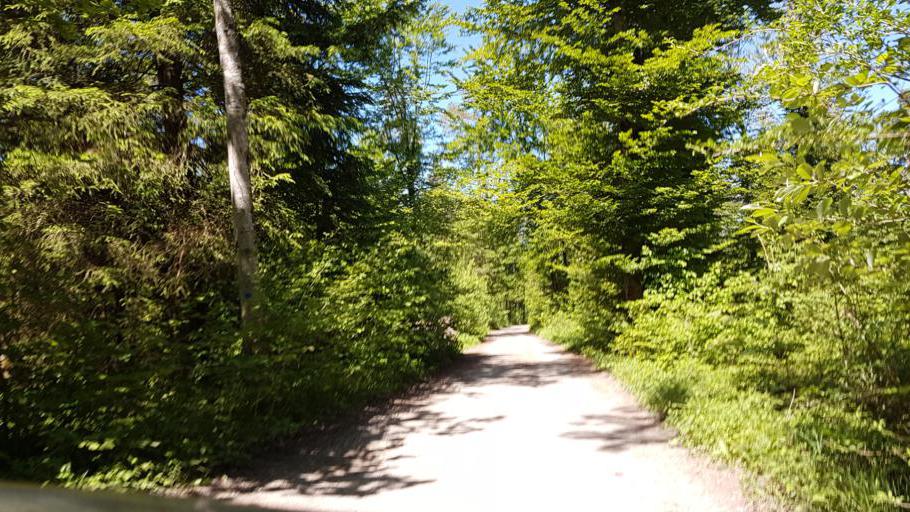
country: CH
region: Bern
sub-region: Thun District
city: Thun
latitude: 46.7152
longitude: 7.6139
